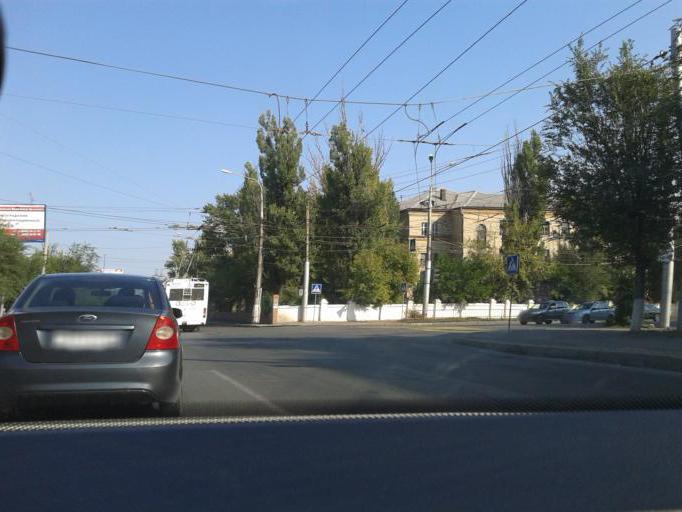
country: RU
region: Volgograd
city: Volgograd
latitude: 48.7344
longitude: 44.4953
